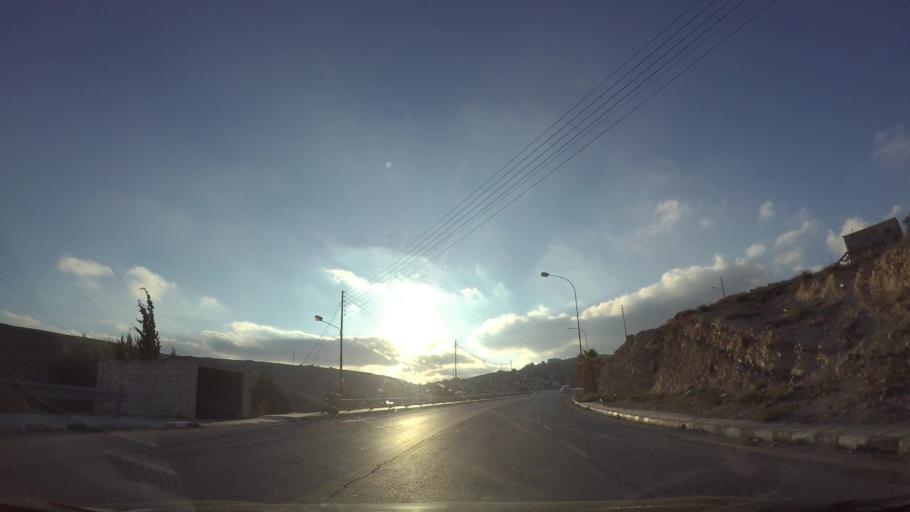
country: JO
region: Ma'an
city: Petra
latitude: 30.5212
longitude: 35.5535
